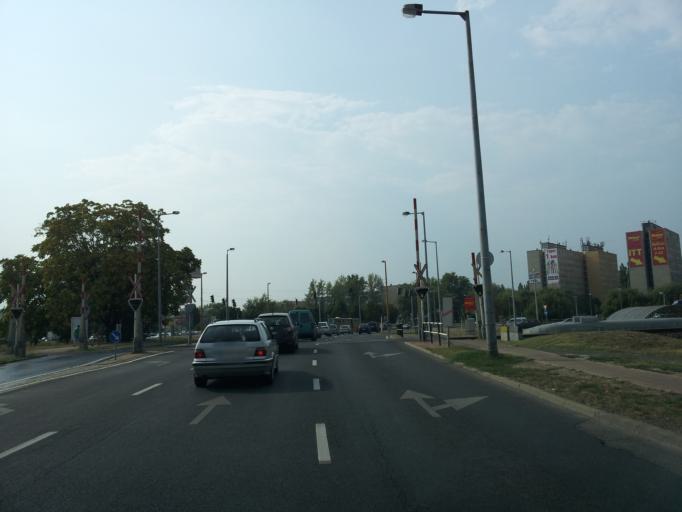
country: HU
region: Gyor-Moson-Sopron
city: Gyor
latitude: 47.6681
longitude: 17.6550
